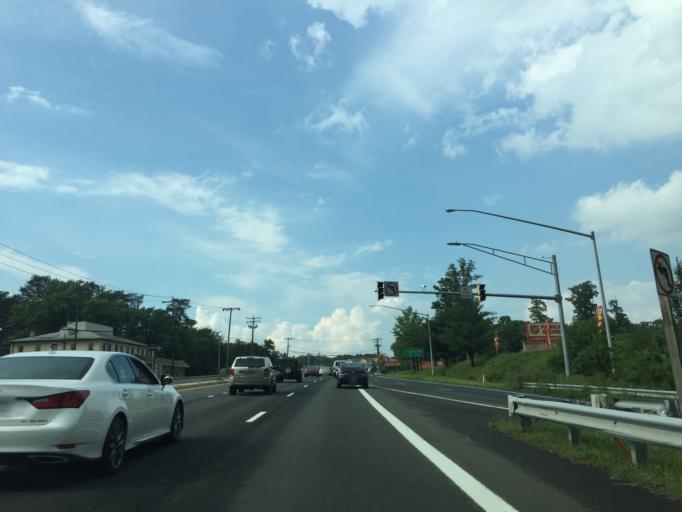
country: US
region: Maryland
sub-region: Howard County
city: Savage
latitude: 39.1419
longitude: -76.8106
